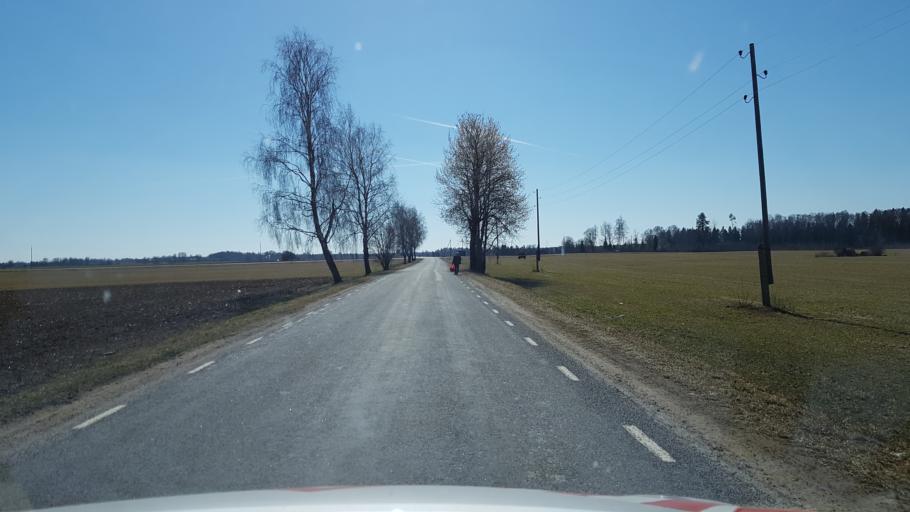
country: EE
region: Laeaene-Virumaa
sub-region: Vaeike-Maarja vald
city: Vaike-Maarja
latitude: 59.0960
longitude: 26.1959
